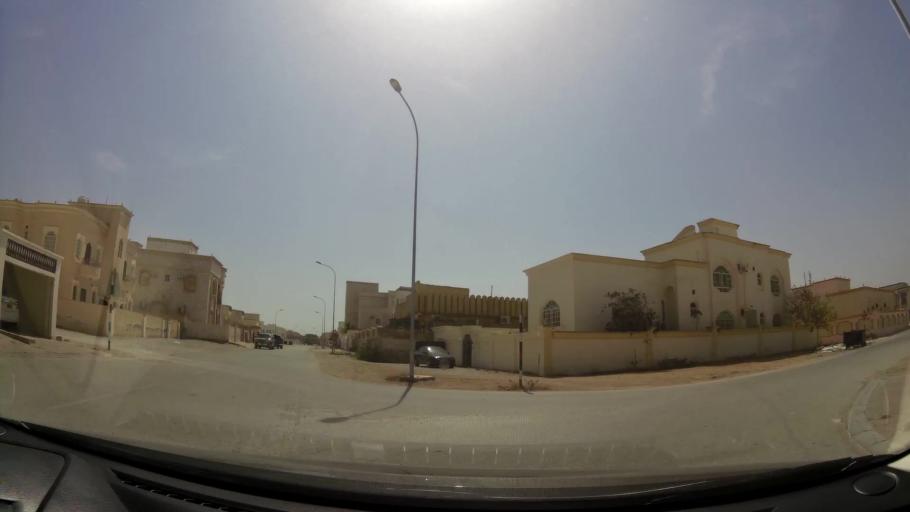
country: OM
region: Zufar
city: Salalah
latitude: 17.0407
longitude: 54.1593
